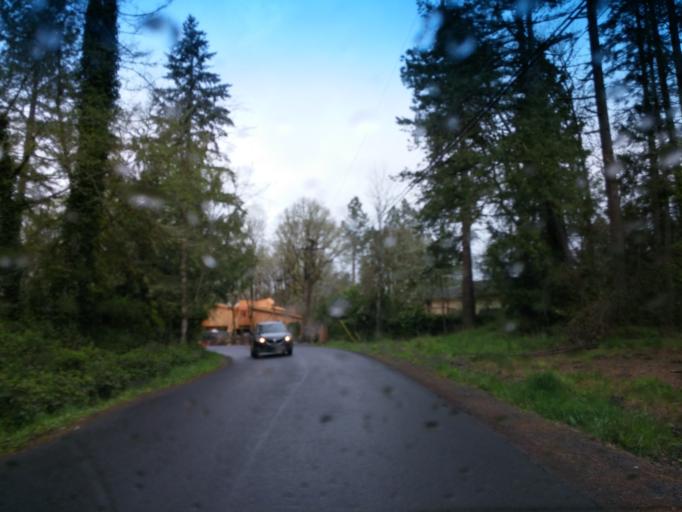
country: US
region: Oregon
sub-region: Washington County
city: Aloha
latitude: 45.5069
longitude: -122.8606
